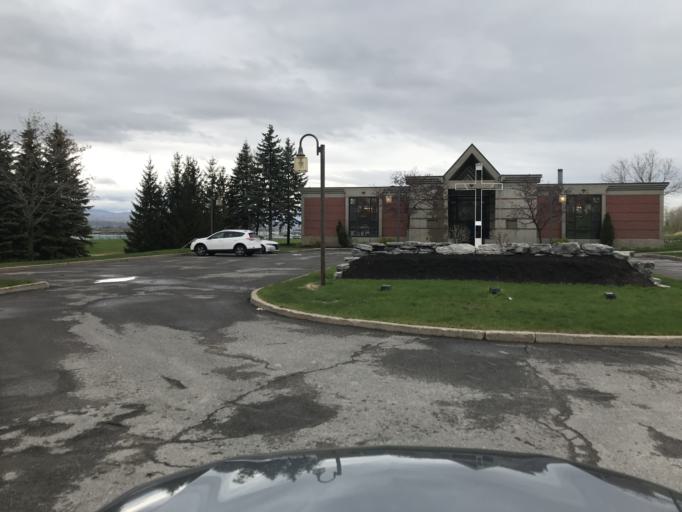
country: CA
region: Quebec
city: L'Ancienne-Lorette
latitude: 46.7914
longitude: -71.2836
